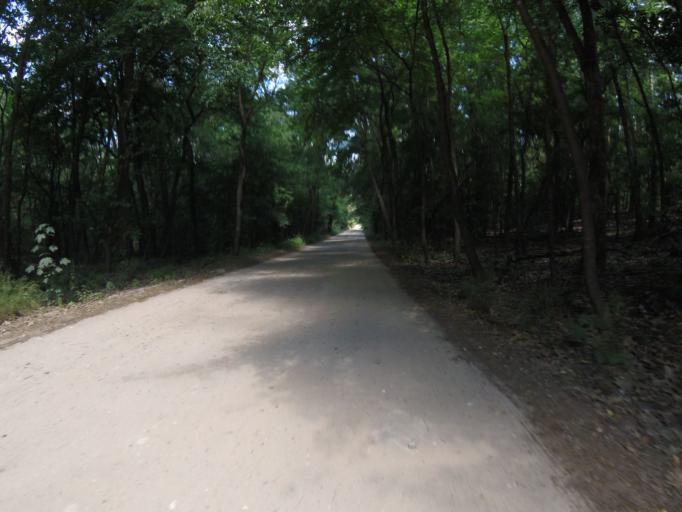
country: DE
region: Brandenburg
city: Bestensee
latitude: 52.2701
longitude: 13.6575
